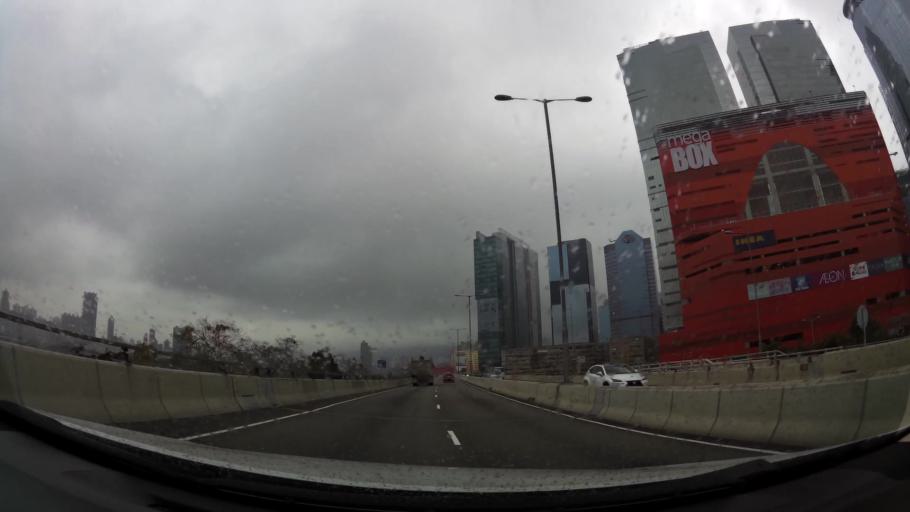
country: HK
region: Kowloon City
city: Kowloon
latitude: 22.3178
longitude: 114.2083
